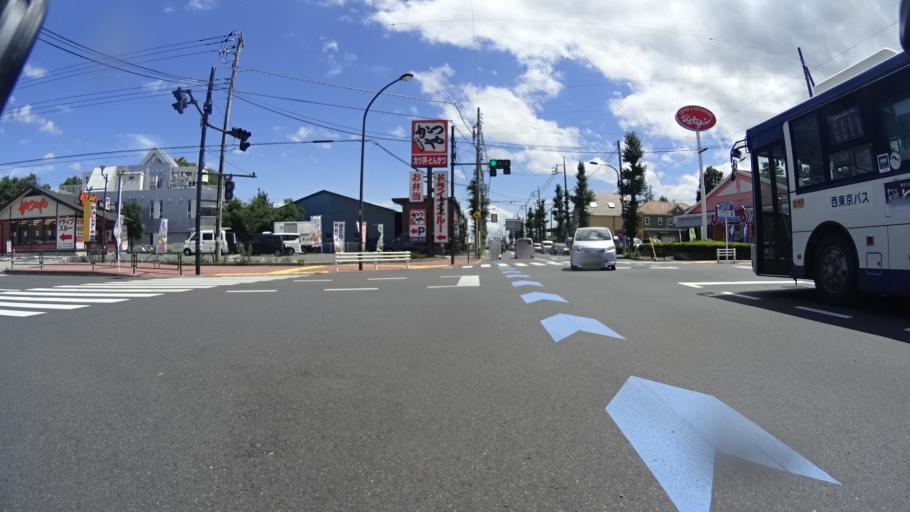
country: JP
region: Tokyo
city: Fussa
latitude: 35.7730
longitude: 139.3023
